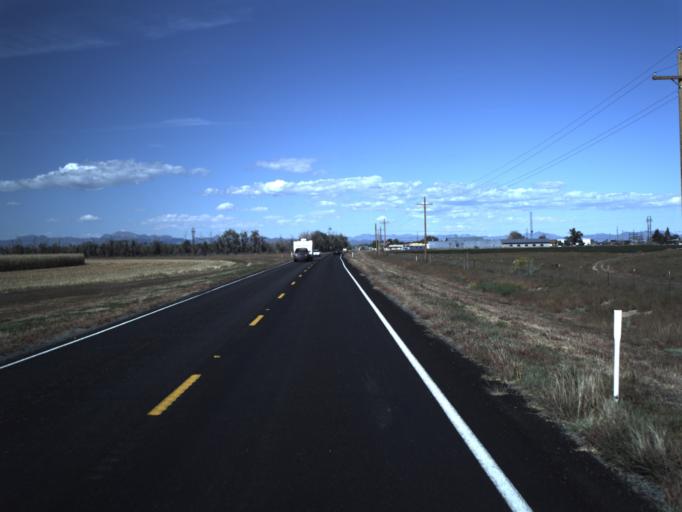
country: US
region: Utah
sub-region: Washington County
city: Enterprise
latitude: 37.7023
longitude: -113.6565
